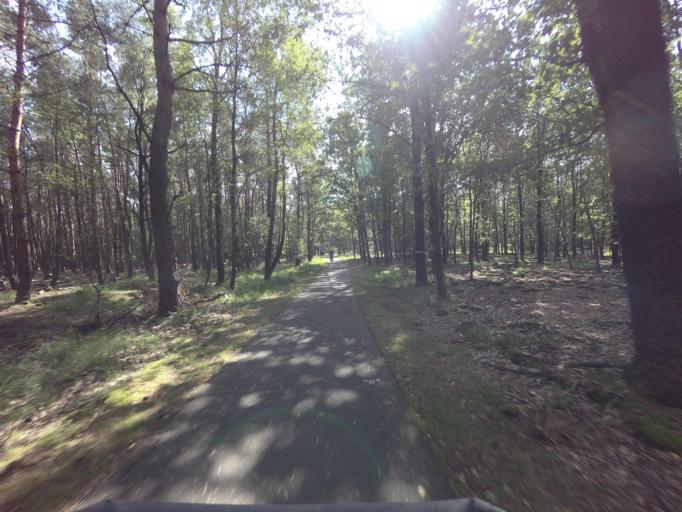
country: NL
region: Drenthe
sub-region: Gemeente Westerveld
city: Dwingeloo
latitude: 52.8068
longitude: 6.4468
